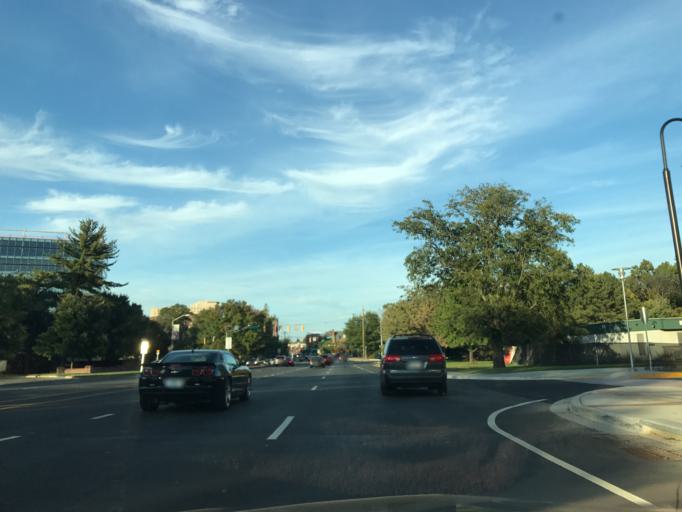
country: US
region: Maryland
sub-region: Prince George's County
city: College Park
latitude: 38.9875
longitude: -76.9357
